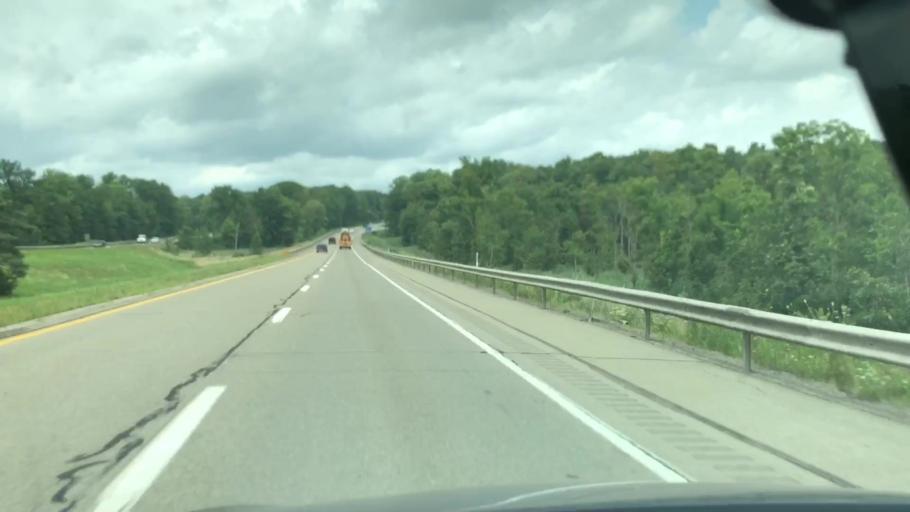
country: US
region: Pennsylvania
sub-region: Erie County
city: Edinboro
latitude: 41.8347
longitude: -80.1756
